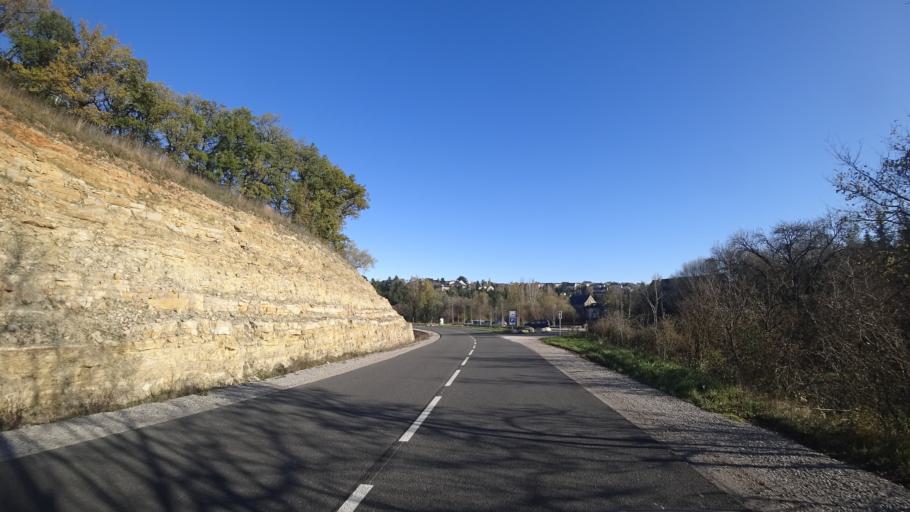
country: FR
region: Midi-Pyrenees
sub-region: Departement de l'Aveyron
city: Rodez
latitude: 44.3791
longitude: 2.5621
